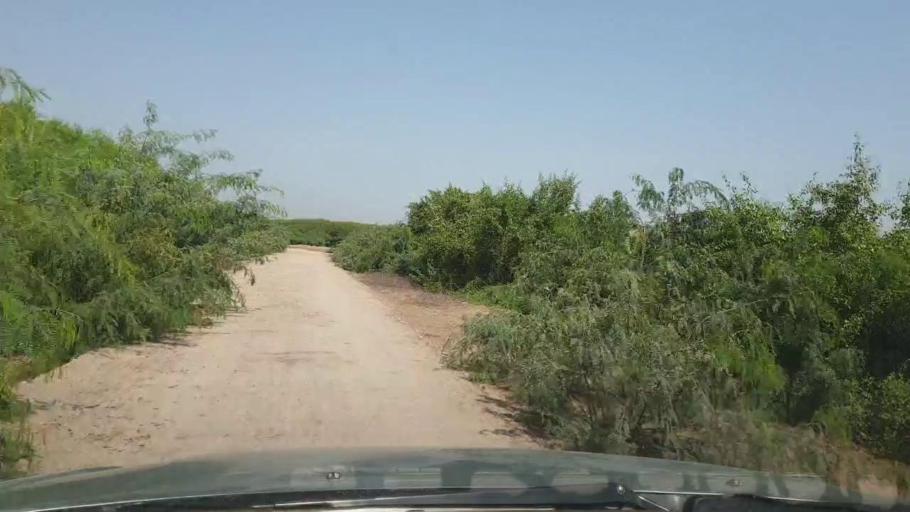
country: PK
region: Sindh
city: Chambar
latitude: 25.2333
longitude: 68.7733
